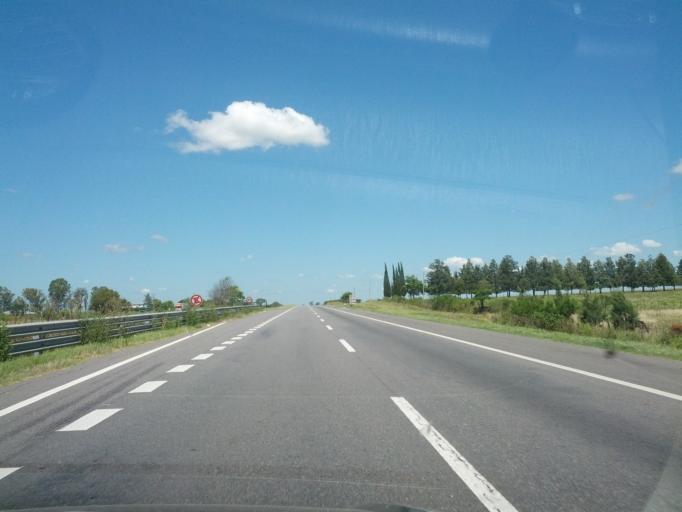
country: AR
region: Entre Rios
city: Gualeguaychu
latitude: -33.1031
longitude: -58.6452
